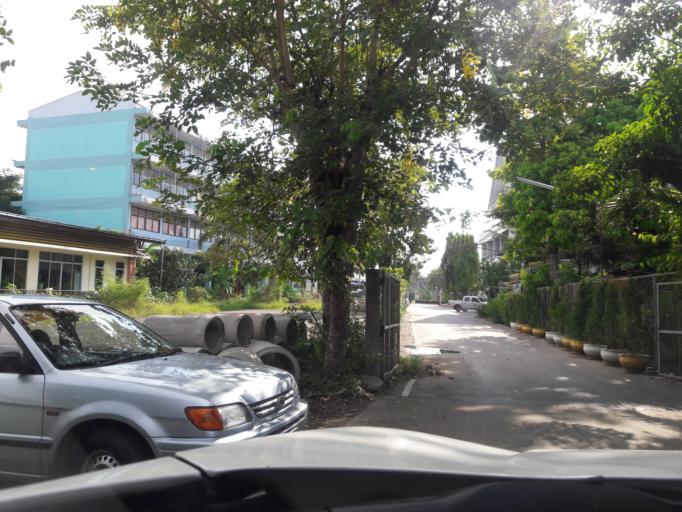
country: TH
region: Lop Buri
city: Ban Mi
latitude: 15.0464
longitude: 100.5365
